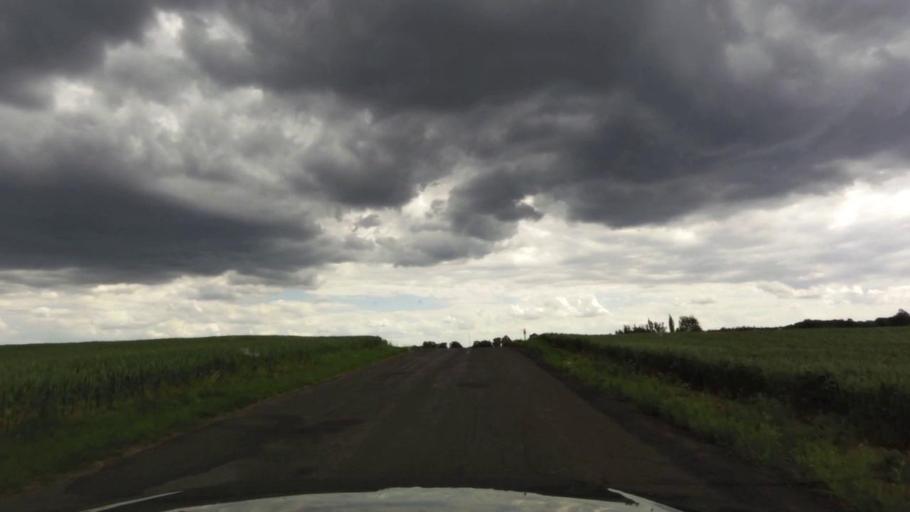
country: PL
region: West Pomeranian Voivodeship
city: Trzcinsko Zdroj
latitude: 52.9201
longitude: 14.5933
